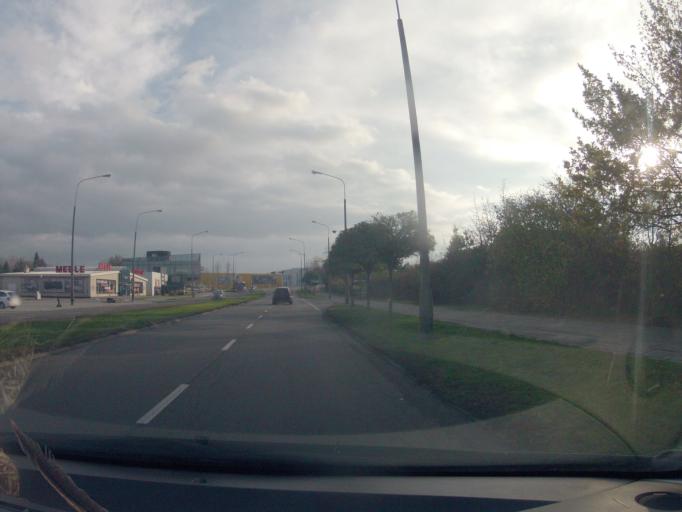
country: PL
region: Opole Voivodeship
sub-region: Powiat opolski
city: Opole
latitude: 50.6705
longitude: 17.9505
